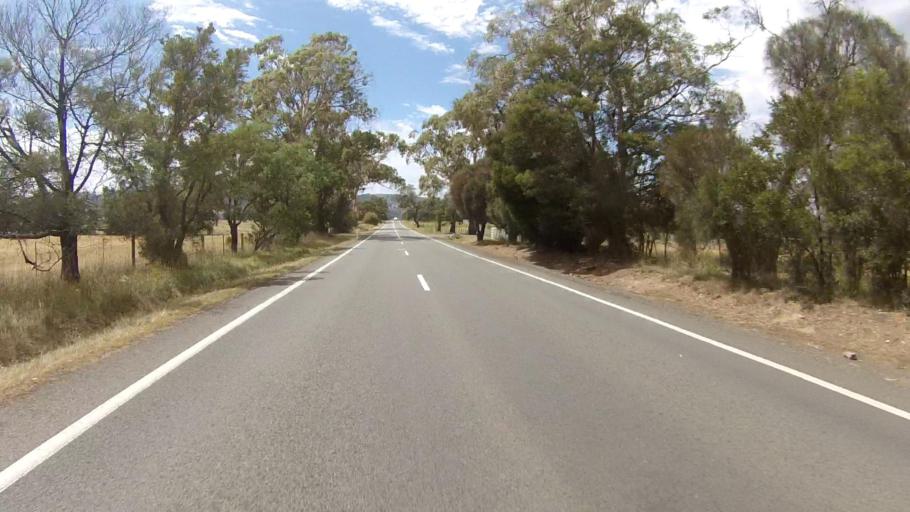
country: AU
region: Tasmania
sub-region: Clarence
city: Cambridge
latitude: -42.6781
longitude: 147.4186
